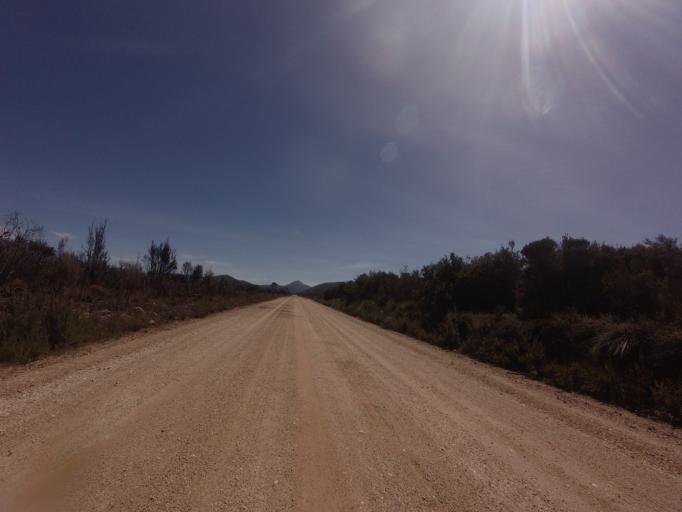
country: AU
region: Tasmania
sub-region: Huon Valley
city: Geeveston
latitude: -42.9725
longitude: 146.3649
